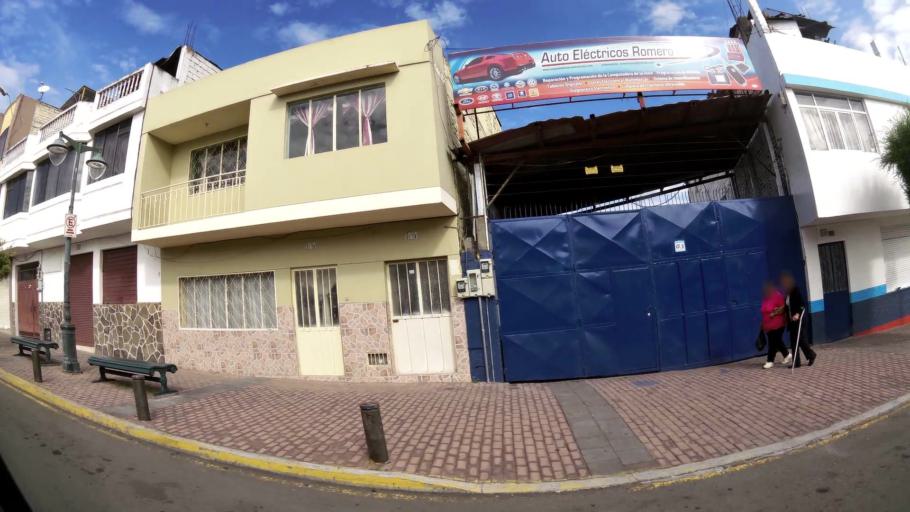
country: EC
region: Tungurahua
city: Ambato
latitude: -1.2384
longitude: -78.6262
